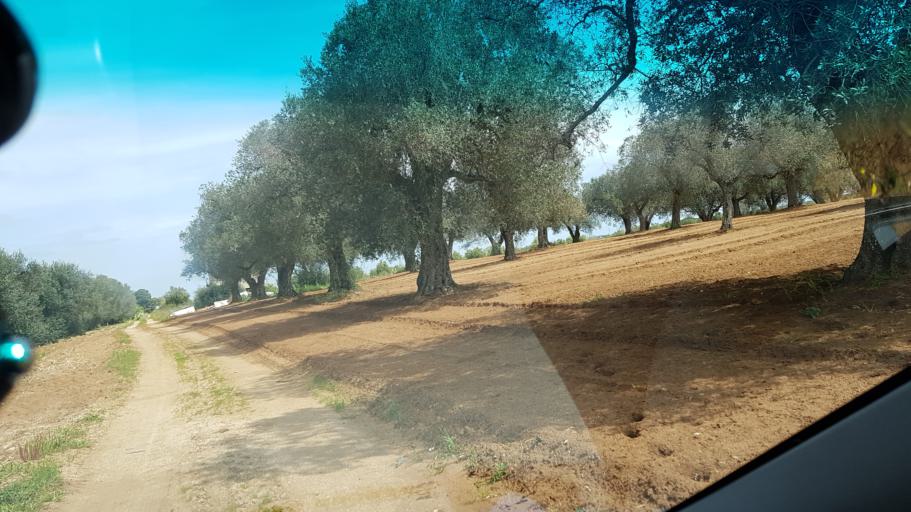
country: IT
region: Apulia
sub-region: Provincia di Brindisi
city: Mesagne
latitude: 40.6090
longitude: 17.8523
